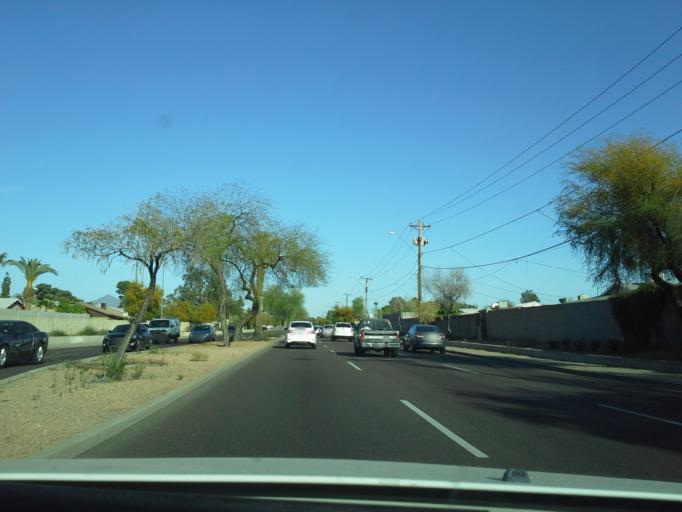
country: US
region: Arizona
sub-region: Maricopa County
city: Paradise Valley
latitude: 33.5971
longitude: -112.0038
